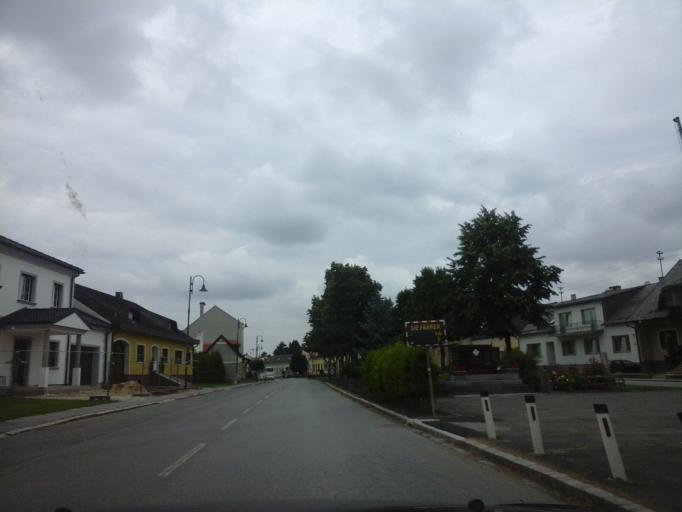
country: AT
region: Lower Austria
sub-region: Politischer Bezirk Ganserndorf
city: Engelhartstetten
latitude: 48.1817
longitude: 16.8852
